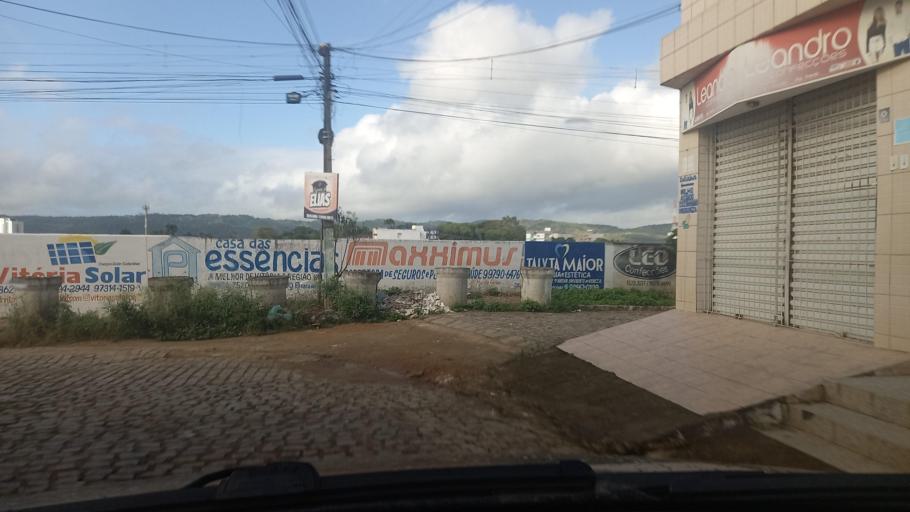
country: BR
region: Pernambuco
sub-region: Vitoria De Santo Antao
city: Vitoria de Santo Antao
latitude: -8.1166
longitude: -35.3079
